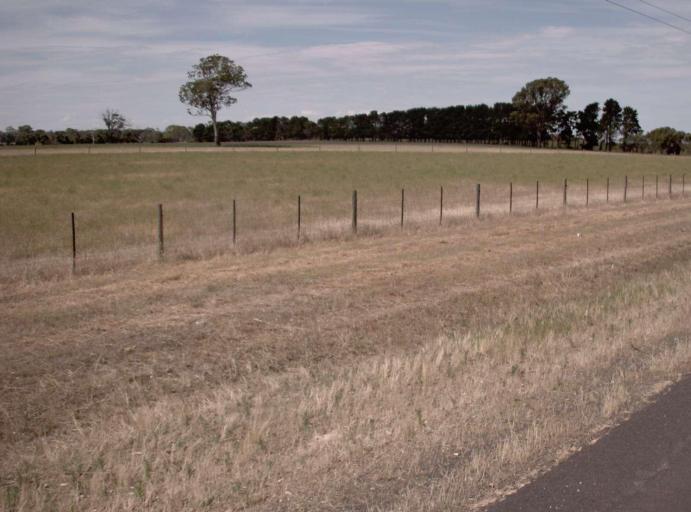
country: AU
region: Victoria
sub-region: Wellington
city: Sale
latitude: -37.9274
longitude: 147.2148
